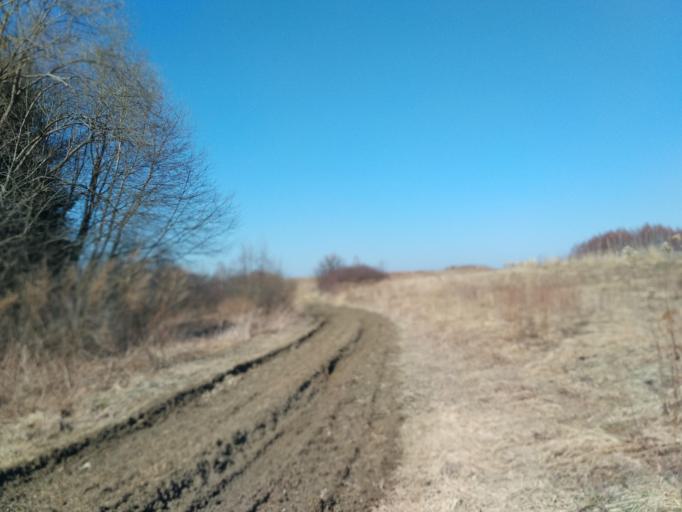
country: PL
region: Subcarpathian Voivodeship
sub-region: Powiat brzozowski
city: Golcowa
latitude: 49.7627
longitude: 22.0315
